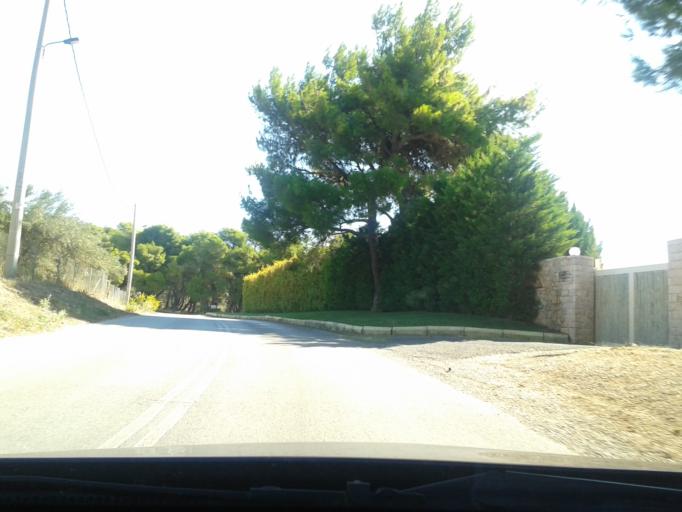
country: GR
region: Attica
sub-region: Nomarchia Anatolikis Attikis
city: Varybobi
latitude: 38.1328
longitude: 23.7792
